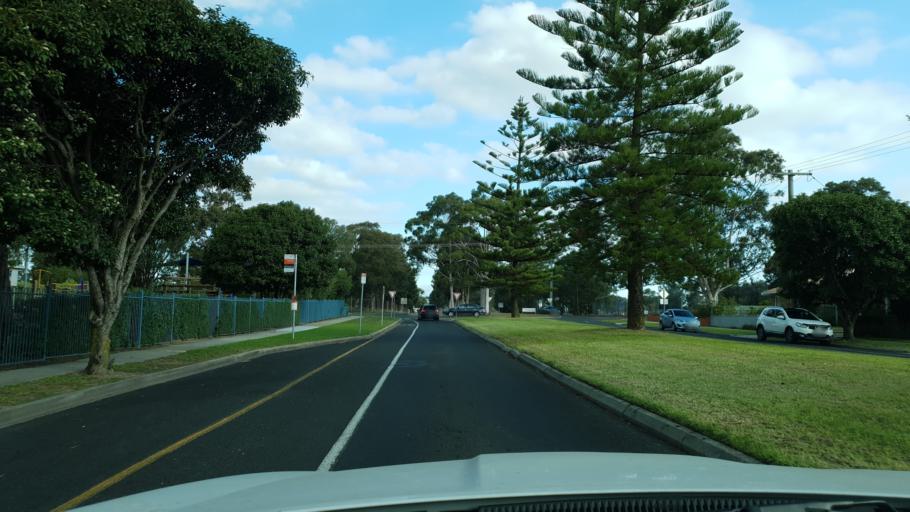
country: AU
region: Victoria
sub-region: East Gippsland
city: Bairnsdale
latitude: -37.8238
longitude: 147.6076
